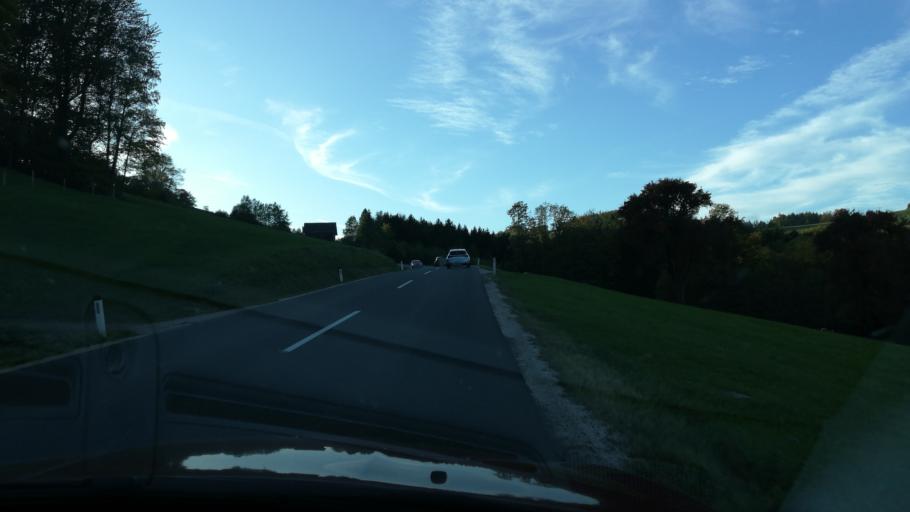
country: AT
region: Upper Austria
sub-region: Politischer Bezirk Kirchdorf an der Krems
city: Gruenburg
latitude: 47.9628
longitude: 14.3091
